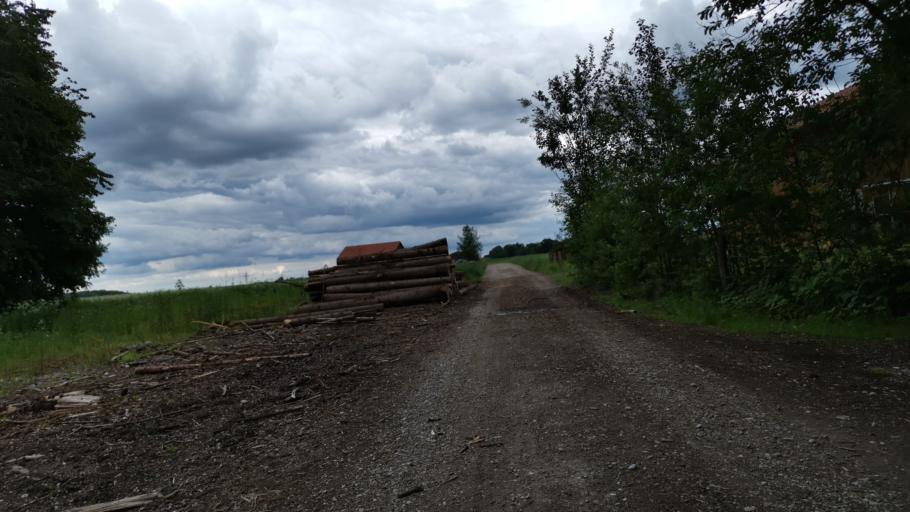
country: DE
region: Bavaria
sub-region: Upper Bavaria
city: Schaftlarn
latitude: 47.9992
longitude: 11.4414
